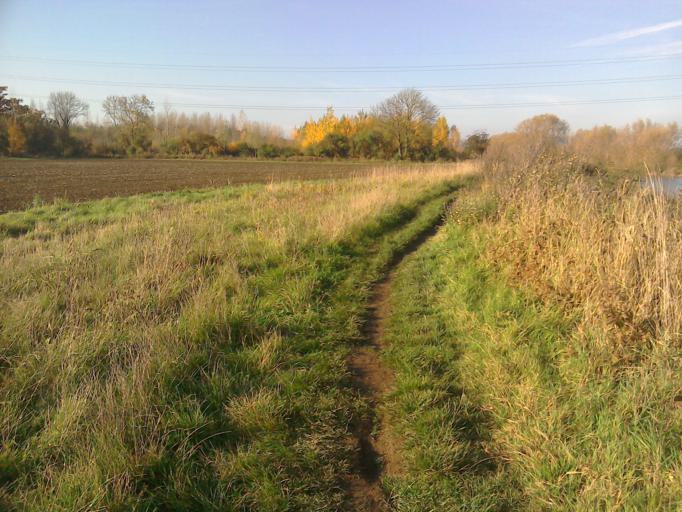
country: GB
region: England
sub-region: Oxfordshire
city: Radley
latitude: 51.6933
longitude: -1.2254
